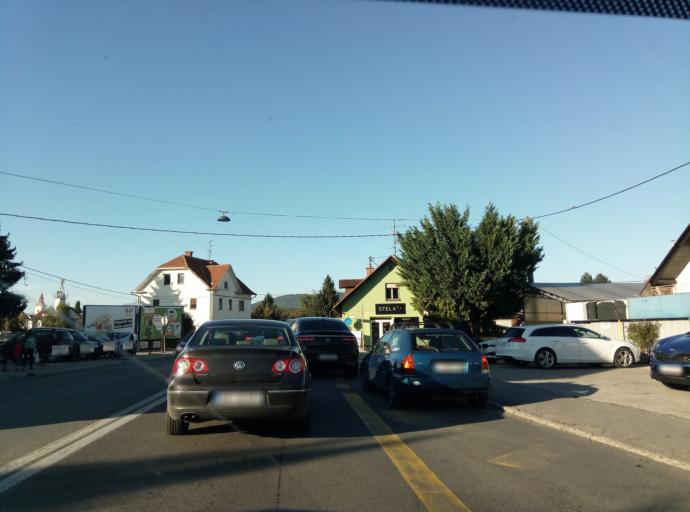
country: SI
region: Ljubljana
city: Ljubljana
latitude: 46.0907
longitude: 14.5140
